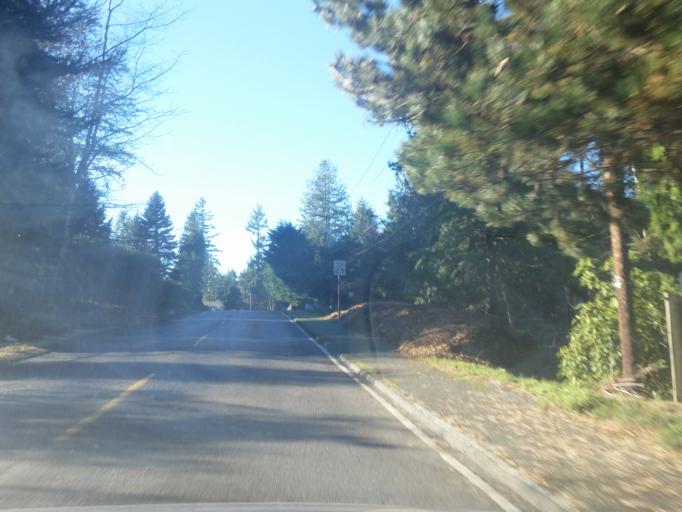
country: US
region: Washington
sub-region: Snohomish County
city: Meadowdale
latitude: 47.8411
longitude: -122.3466
